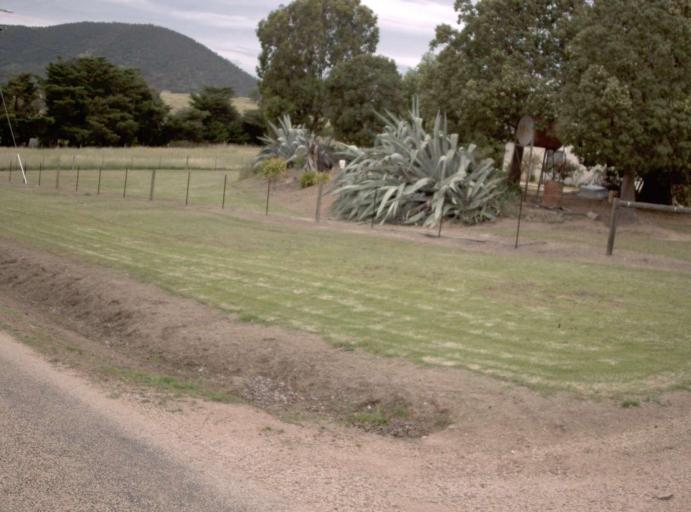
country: AU
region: Victoria
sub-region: East Gippsland
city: Bairnsdale
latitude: -37.4718
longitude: 147.2467
